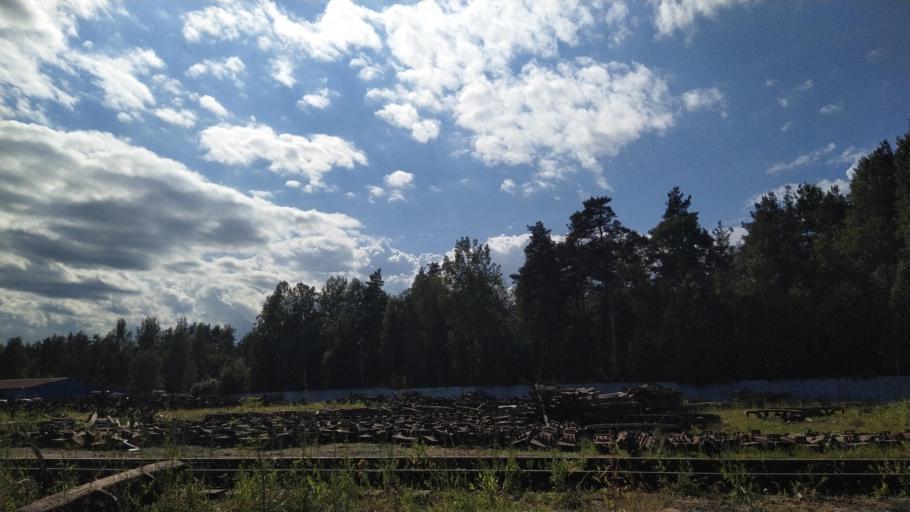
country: RU
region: St.-Petersburg
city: Bol'shaya Izhora
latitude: 59.9170
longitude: 29.5789
